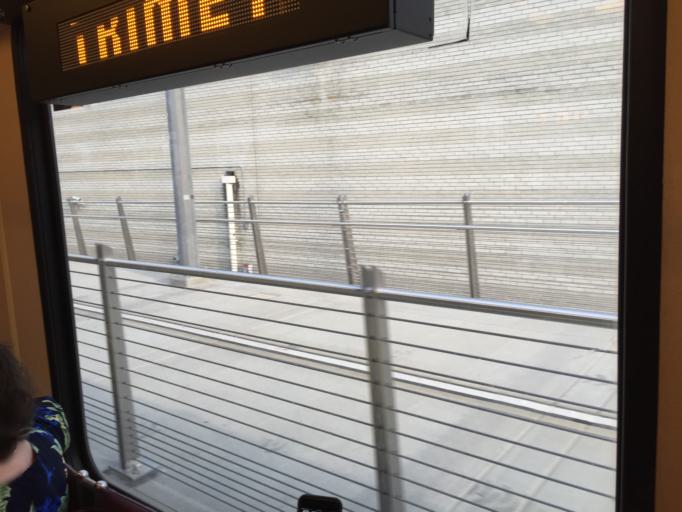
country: US
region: Oregon
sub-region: Multnomah County
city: Portland
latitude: 45.5065
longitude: -122.6642
